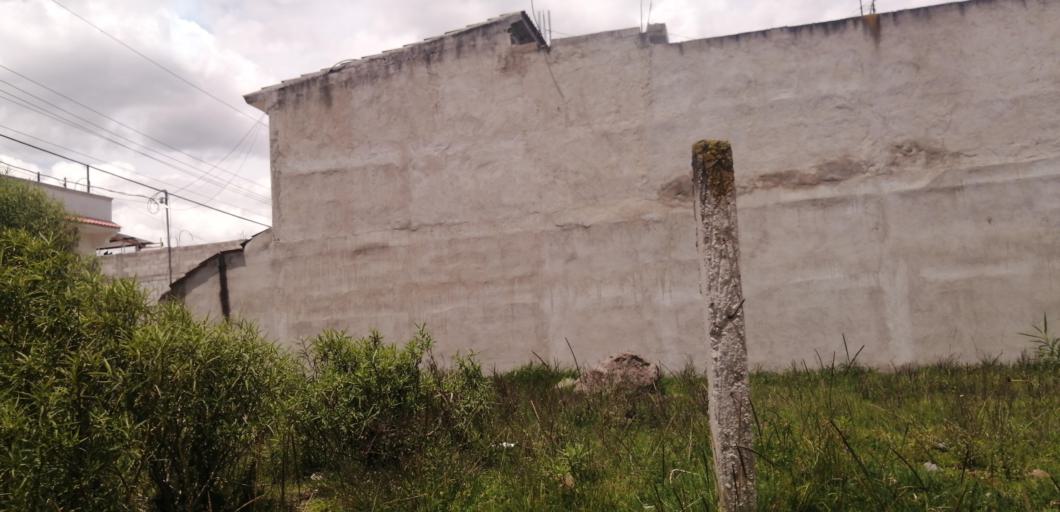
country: GT
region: Quetzaltenango
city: Quetzaltenango
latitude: 14.8291
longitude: -91.5312
